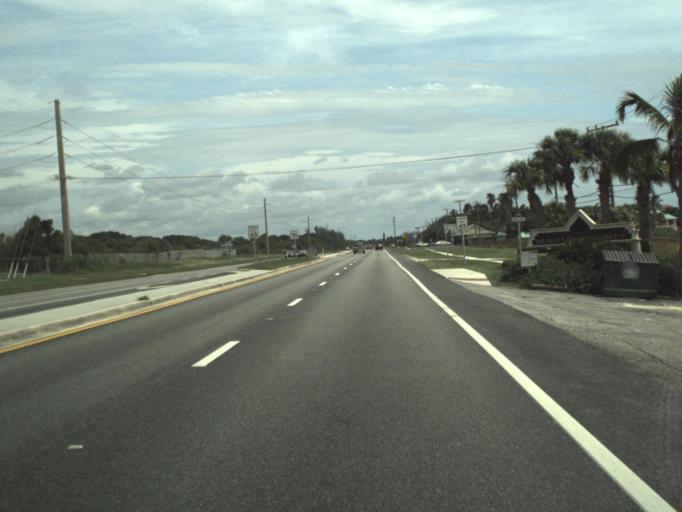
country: US
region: Florida
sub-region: Palm Beach County
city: Jupiter
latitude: 26.9708
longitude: -80.0873
